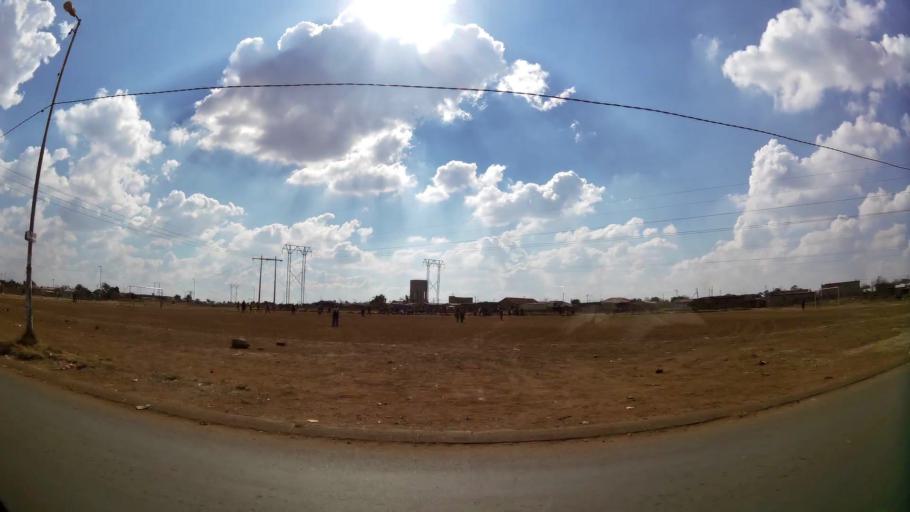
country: ZA
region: Gauteng
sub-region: City of Johannesburg Metropolitan Municipality
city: Roodepoort
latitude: -26.1902
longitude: 27.8569
